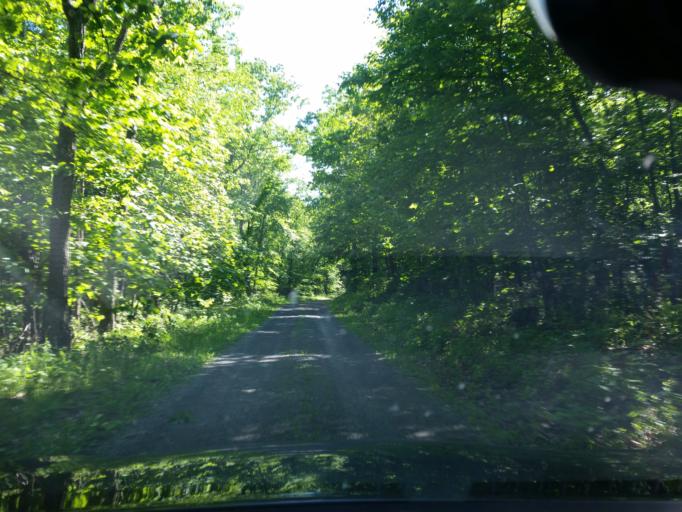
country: US
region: Pennsylvania
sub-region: Lycoming County
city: Duboistown
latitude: 41.1197
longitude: -77.1174
